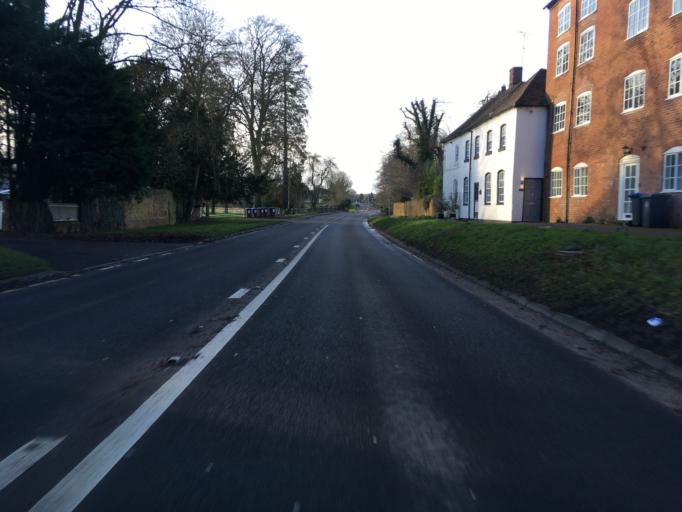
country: GB
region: England
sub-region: Warwickshire
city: Henley in Arden
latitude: 52.2660
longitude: -1.7720
